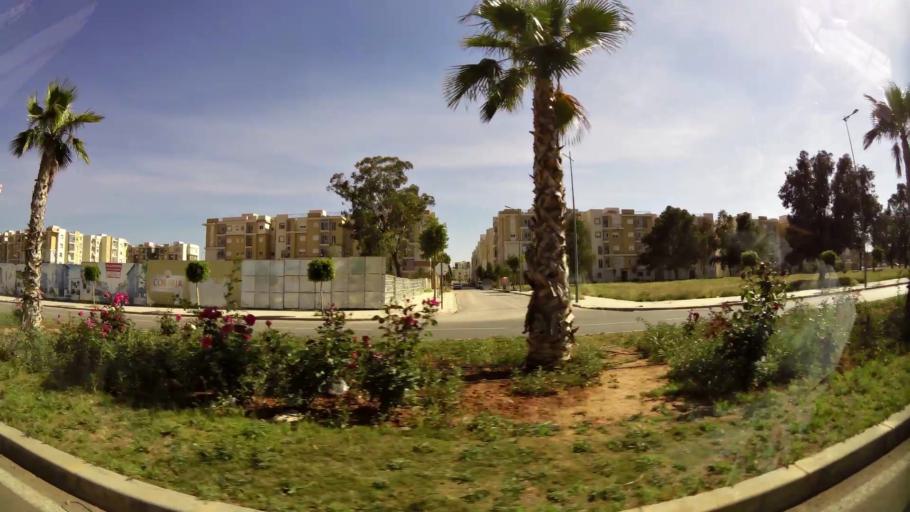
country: MA
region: Oriental
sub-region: Oujda-Angad
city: Oujda
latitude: 34.6645
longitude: -1.9162
